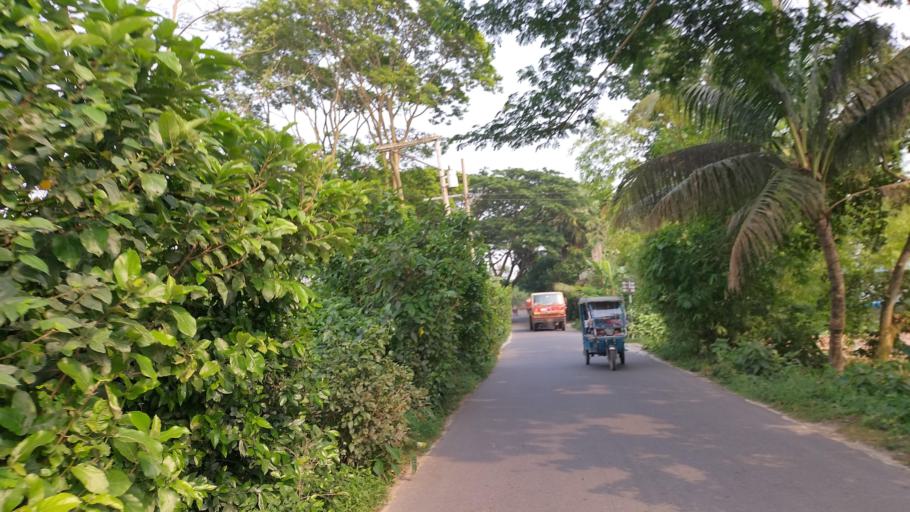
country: BD
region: Dhaka
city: Azimpur
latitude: 23.6771
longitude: 90.3167
